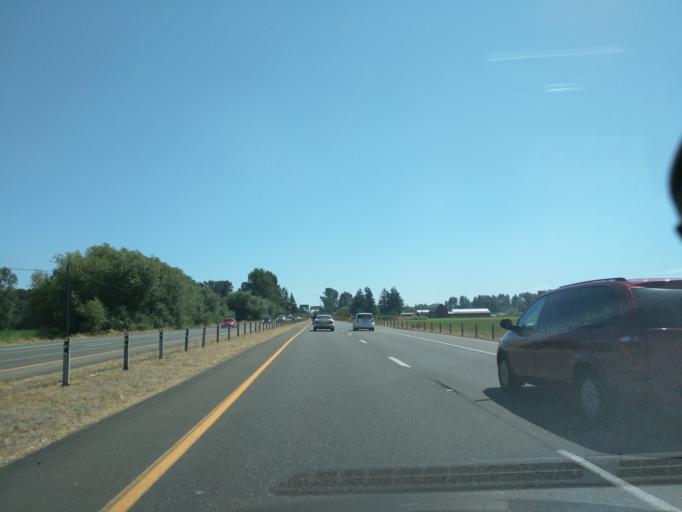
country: US
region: Washington
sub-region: Whatcom County
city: Lynden
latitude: 48.9268
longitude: -122.4857
